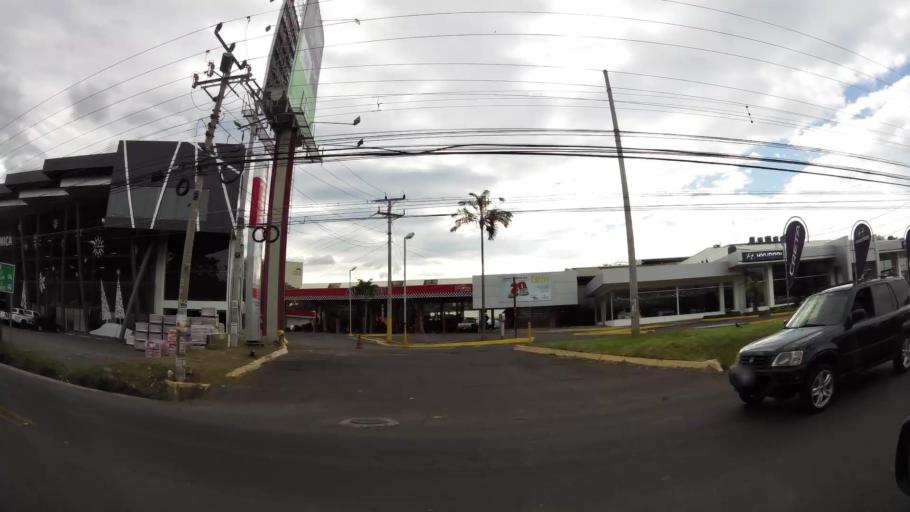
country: CR
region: San Jose
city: Santa Ana
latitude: 9.9473
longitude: -84.1920
